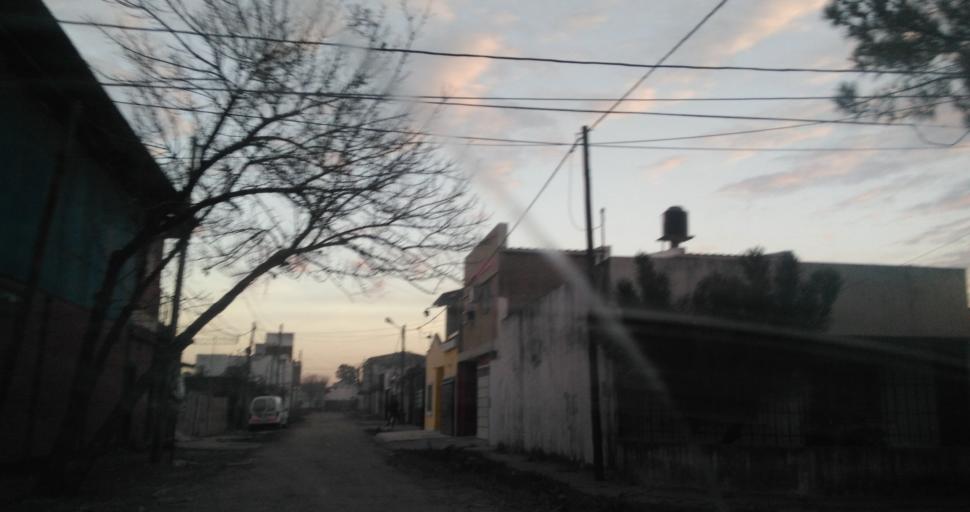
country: AR
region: Chaco
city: Resistencia
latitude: -27.4610
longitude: -59.0097
